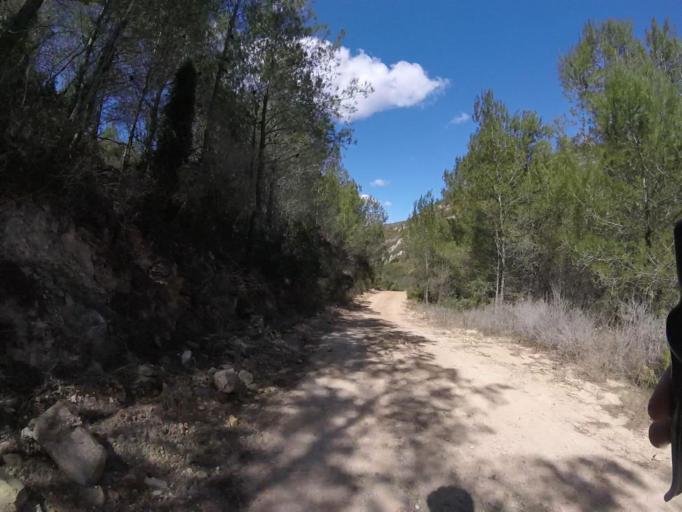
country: ES
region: Valencia
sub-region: Provincia de Castello
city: Cabanes
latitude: 40.1608
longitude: 0.1075
